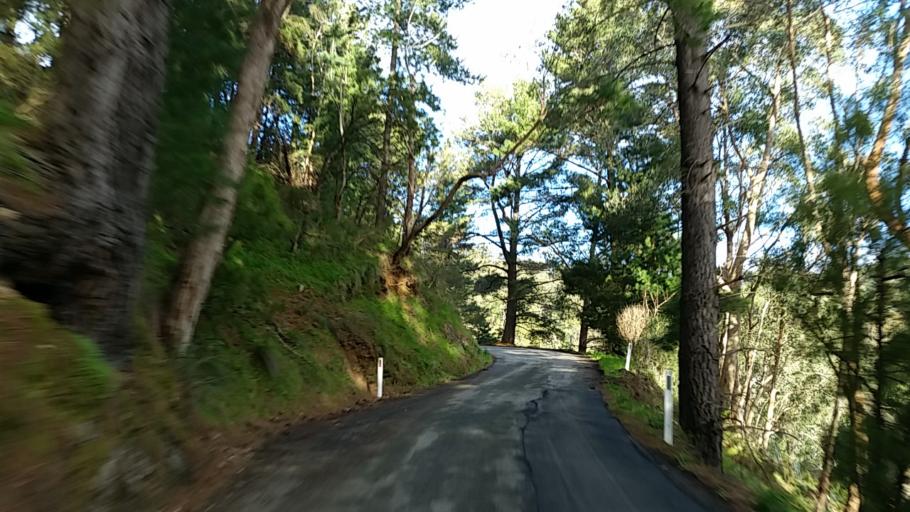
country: AU
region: South Australia
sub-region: Adelaide Hills
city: Adelaide Hills
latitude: -34.9289
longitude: 138.7742
